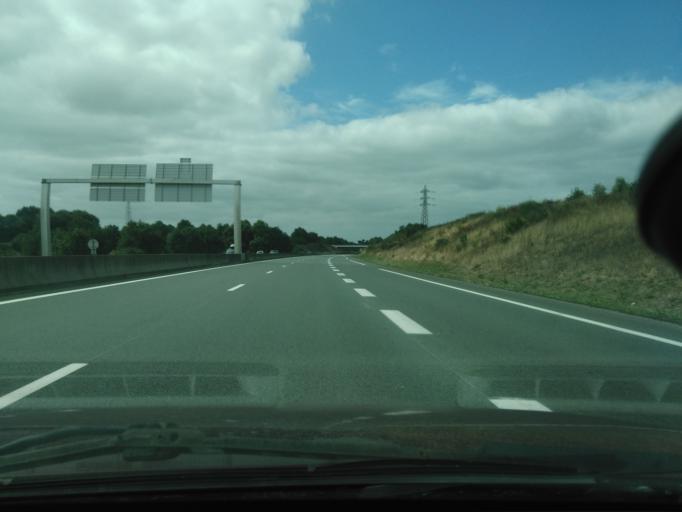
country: FR
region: Pays de la Loire
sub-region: Departement de la Vendee
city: Nesmy
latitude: 46.6346
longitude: -1.4014
